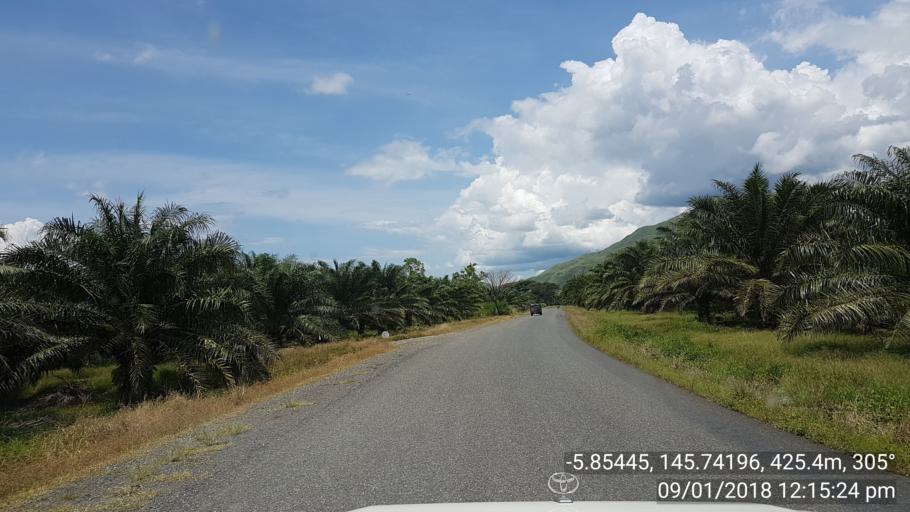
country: PG
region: Eastern Highlands
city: Goroka
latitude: -5.8544
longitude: 145.7419
